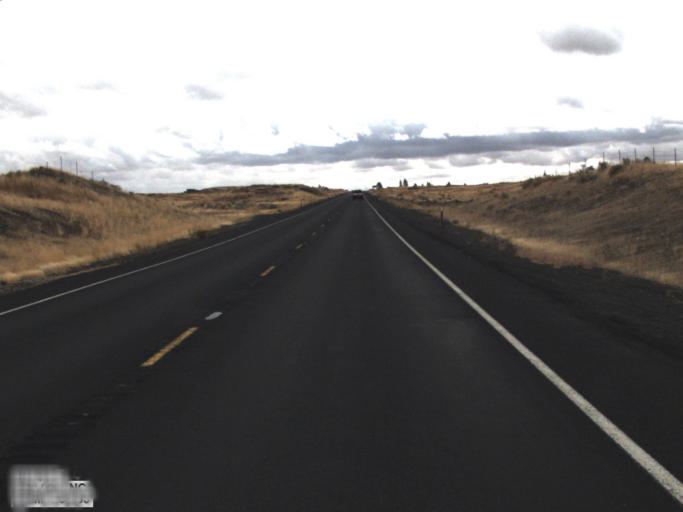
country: US
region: Washington
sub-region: Lincoln County
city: Davenport
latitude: 47.7080
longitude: -118.4213
